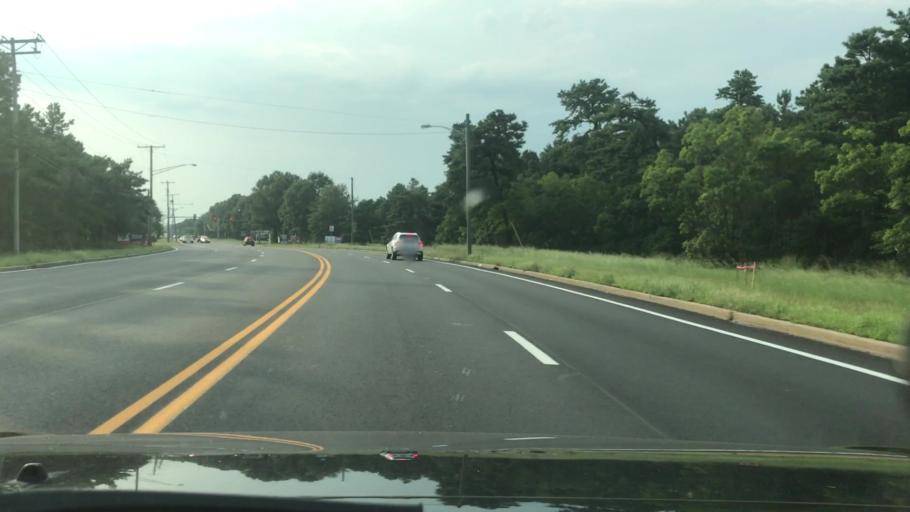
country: US
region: New Jersey
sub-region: Ocean County
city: Leisure Village
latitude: 40.0679
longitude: -74.1651
